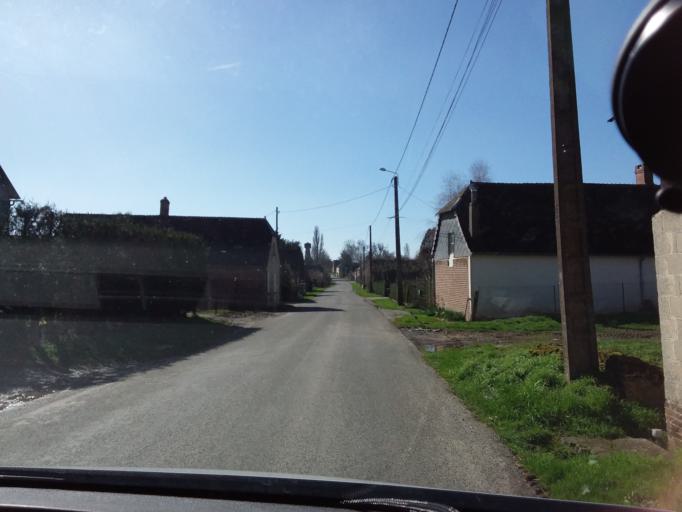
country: FR
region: Picardie
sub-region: Departement de l'Aisne
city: Montcornet
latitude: 49.7570
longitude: 4.0024
